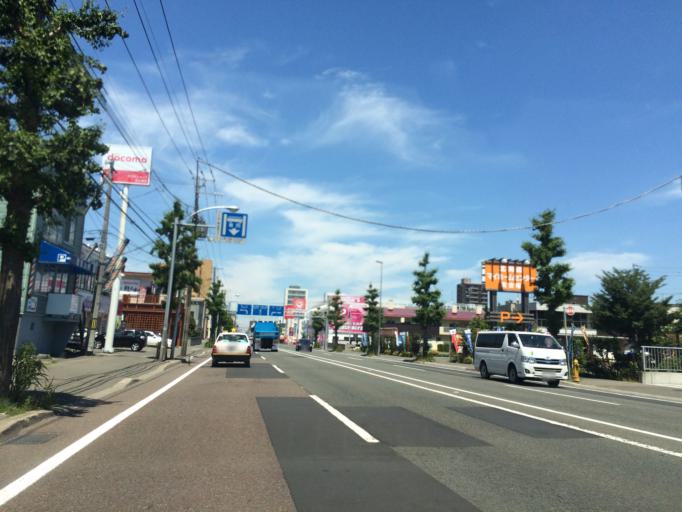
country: JP
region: Hokkaido
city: Sapporo
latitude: 43.0282
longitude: 141.3452
